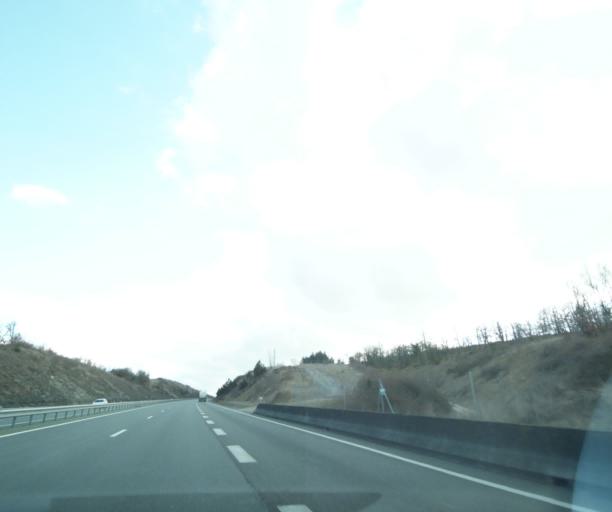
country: FR
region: Midi-Pyrenees
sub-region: Departement du Lot
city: Le Vigan
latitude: 44.7176
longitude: 1.5663
